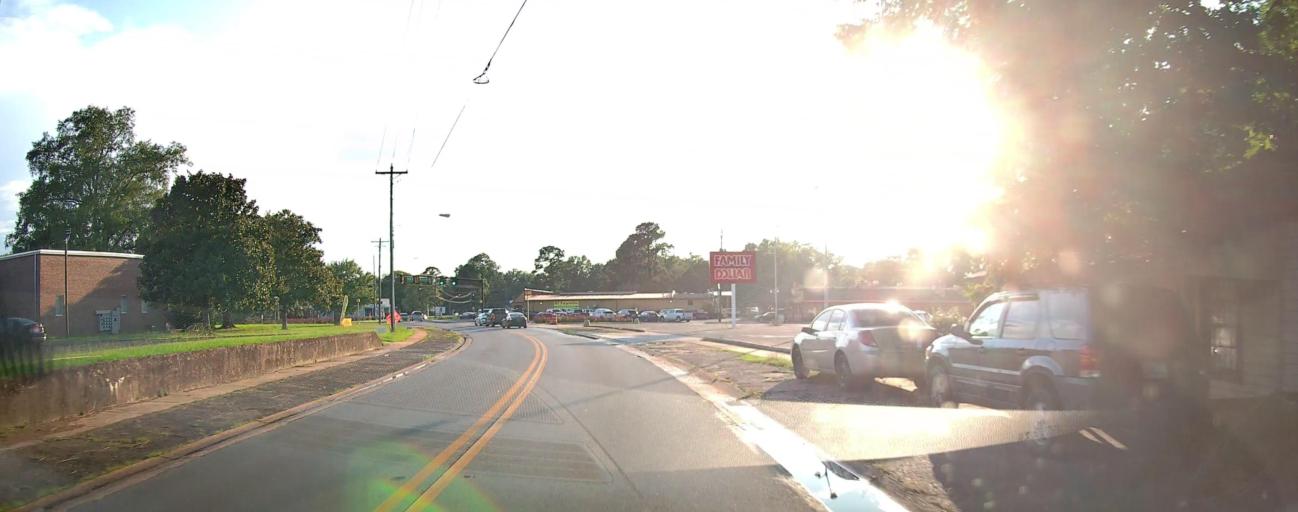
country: US
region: Georgia
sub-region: Peach County
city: Fort Valley
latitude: 32.5592
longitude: -83.8923
